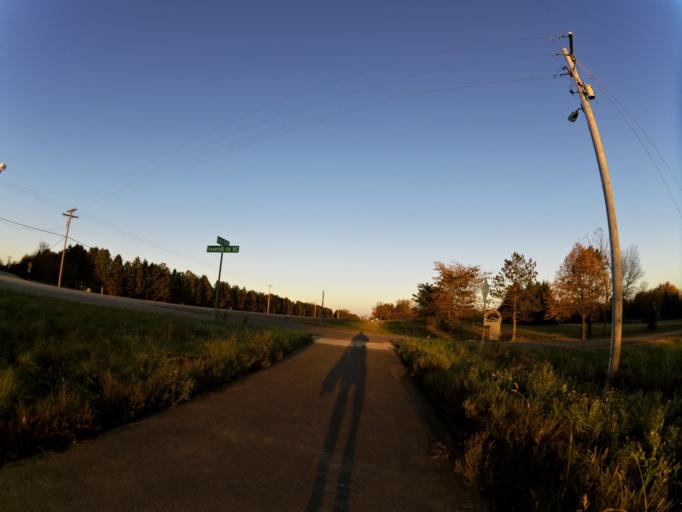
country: US
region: Minnesota
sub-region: Olmsted County
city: Rochester
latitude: 44.0490
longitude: -92.4090
